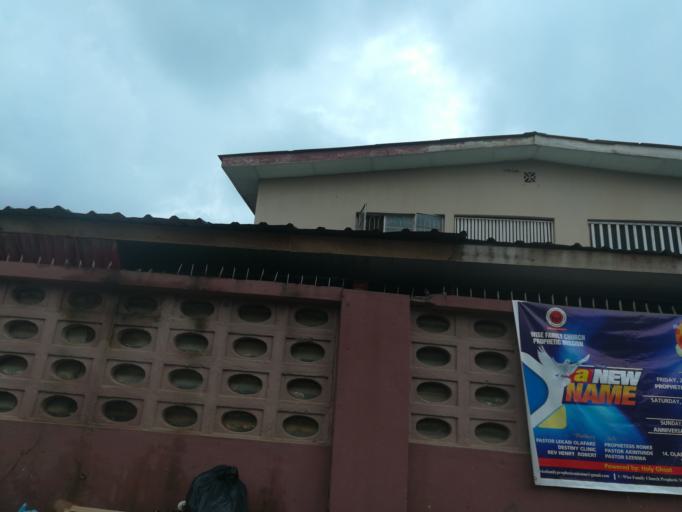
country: NG
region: Lagos
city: Agege
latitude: 6.6050
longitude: 3.3121
